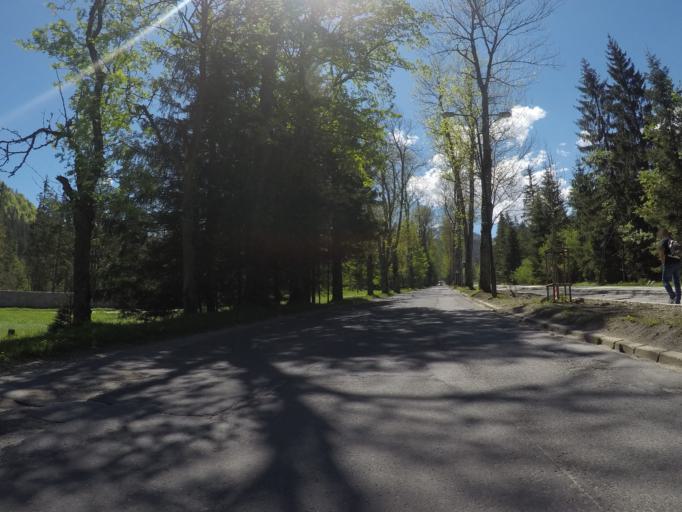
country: PL
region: Lesser Poland Voivodeship
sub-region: Powiat tatrzanski
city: Zakopane
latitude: 49.2776
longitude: 19.9809
